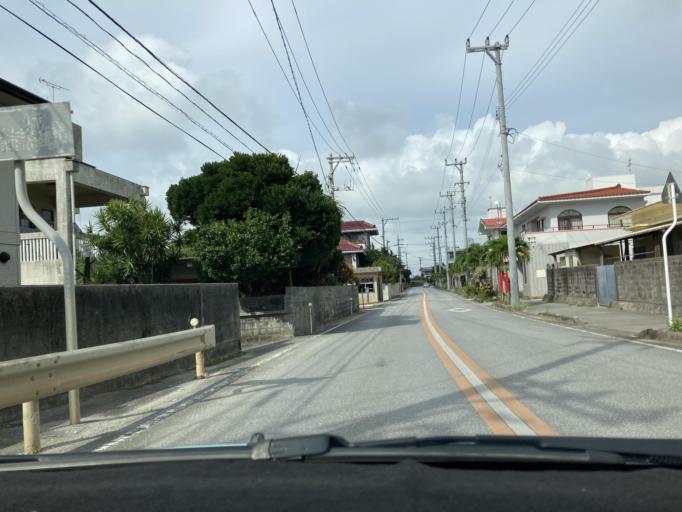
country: JP
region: Okinawa
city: Itoman
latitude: 26.1062
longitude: 127.6647
